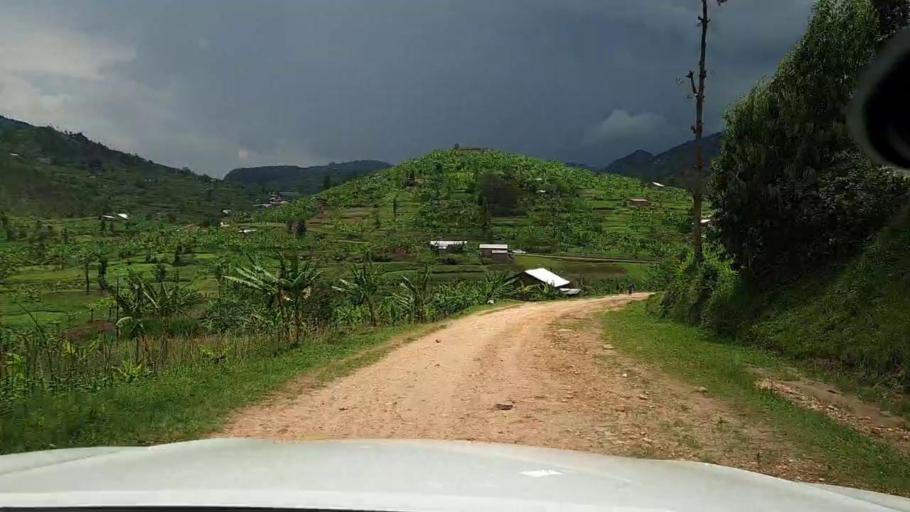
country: RW
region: Western Province
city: Kibuye
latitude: -2.0726
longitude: 29.4345
